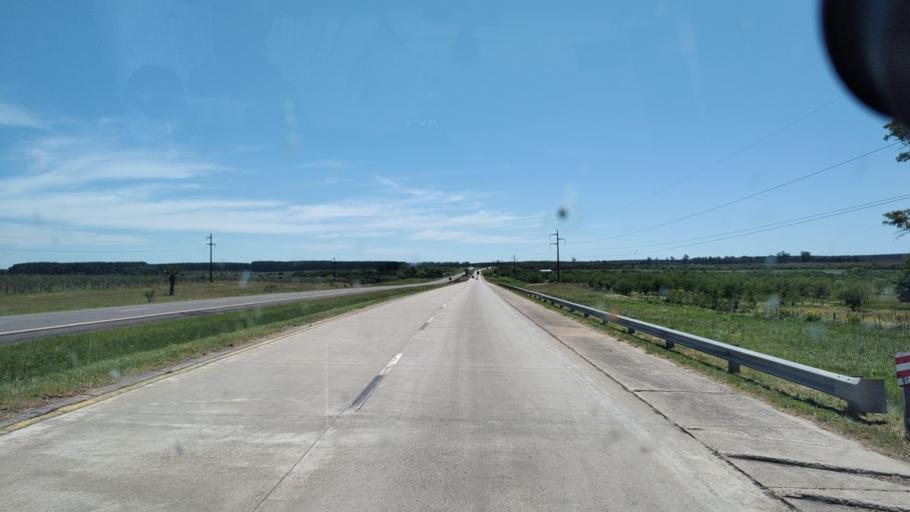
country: AR
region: Entre Rios
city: Ubajay
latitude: -31.9763
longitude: -58.3055
